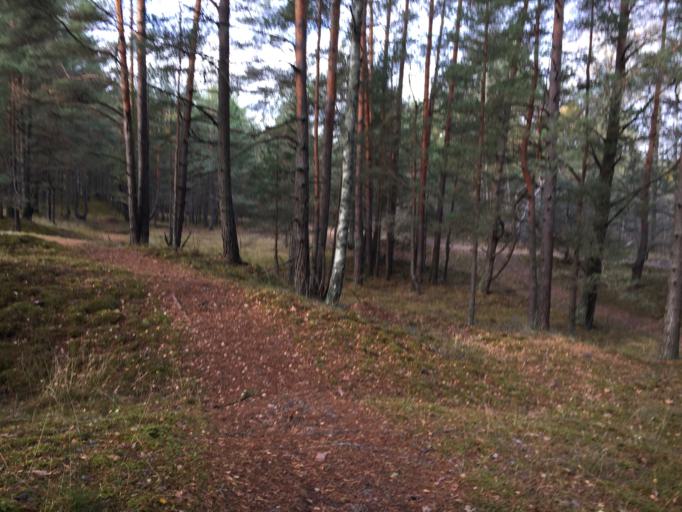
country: LV
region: Carnikava
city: Carnikava
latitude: 57.1491
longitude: 24.2610
